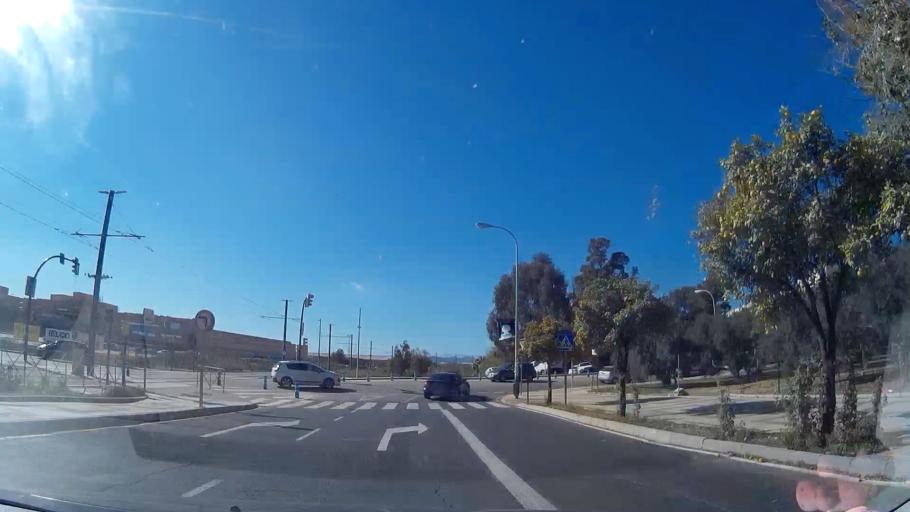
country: ES
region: Andalusia
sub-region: Provincia de Malaga
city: Malaga
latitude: 36.7166
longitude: -4.4756
